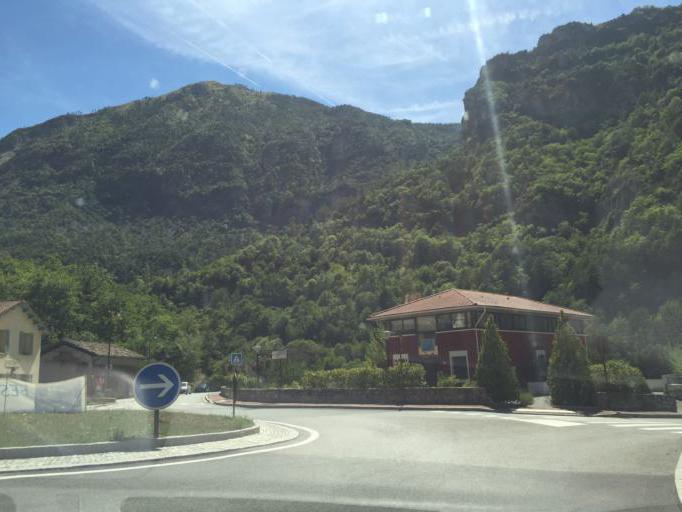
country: FR
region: Provence-Alpes-Cote d'Azur
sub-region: Departement des Alpes-Maritimes
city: Gilette
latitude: 43.9766
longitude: 7.1402
